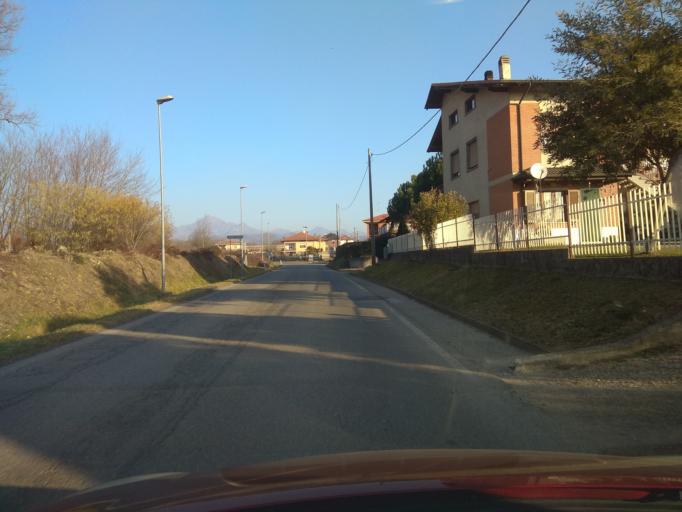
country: IT
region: Piedmont
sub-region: Provincia di Biella
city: Brusnengo
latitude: 45.5831
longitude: 8.2519
